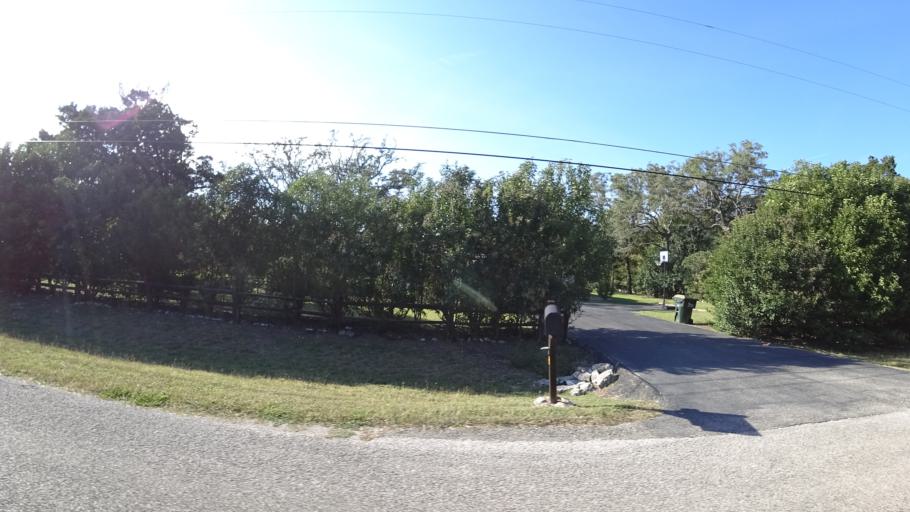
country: US
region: Texas
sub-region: Travis County
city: Barton Creek
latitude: 30.2463
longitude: -97.9131
